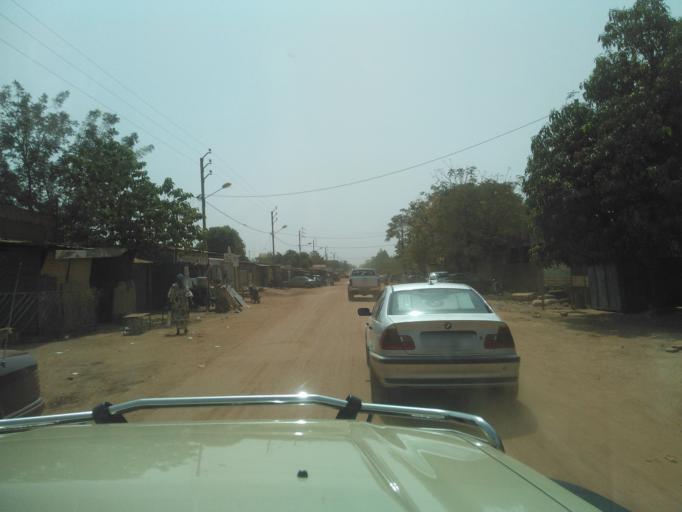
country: BF
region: Centre
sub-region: Kadiogo Province
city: Ouagadougou
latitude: 12.3901
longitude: -1.4754
